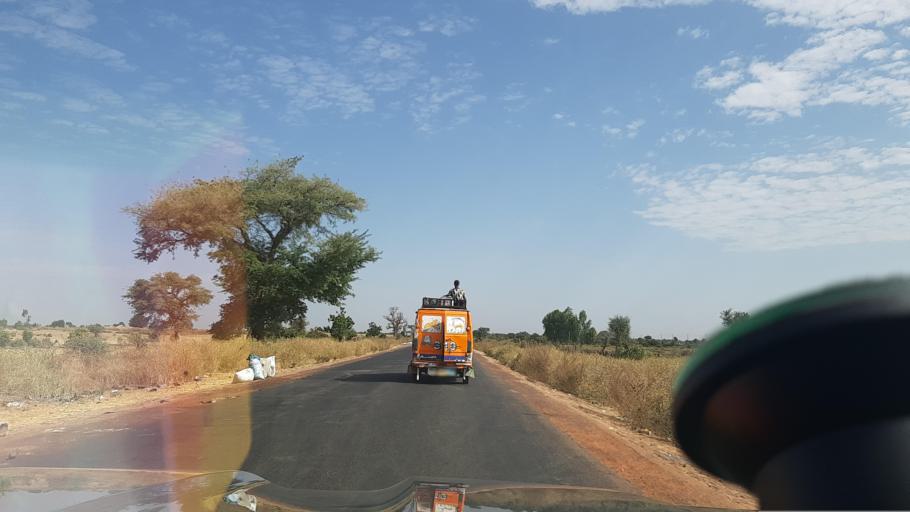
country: ML
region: Segou
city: Markala
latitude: 13.6929
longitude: -6.0994
